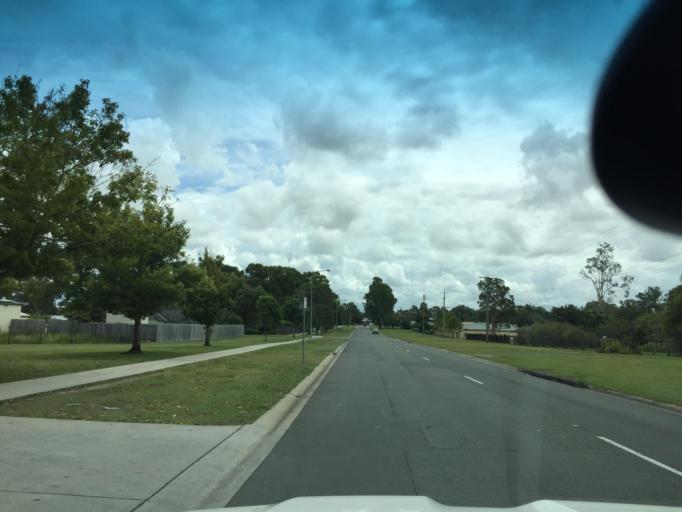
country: AU
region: Queensland
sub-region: Moreton Bay
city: Burpengary
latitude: -27.1365
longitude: 152.9831
